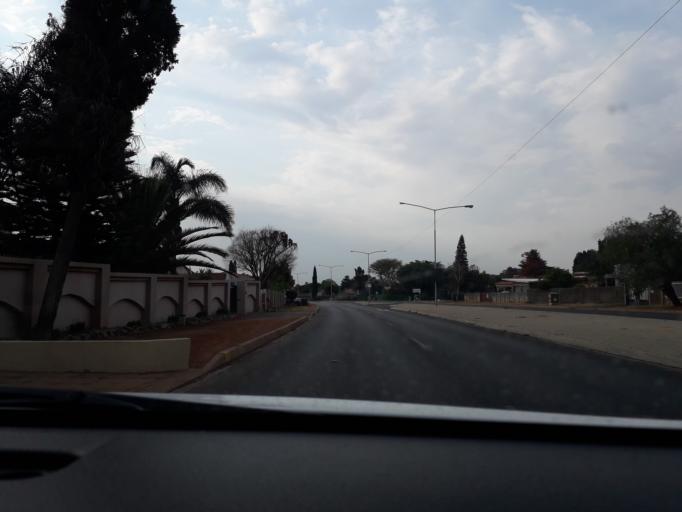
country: ZA
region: Gauteng
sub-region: City of Johannesburg Metropolitan Municipality
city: Modderfontein
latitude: -26.0623
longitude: 28.2061
